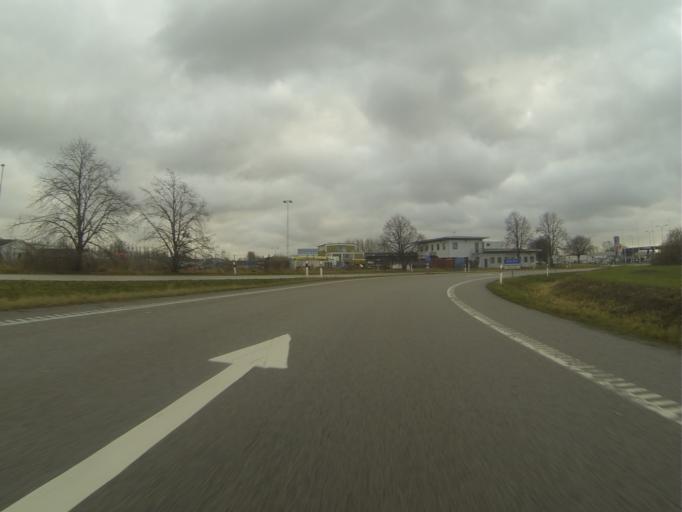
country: SE
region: Skane
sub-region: Burlovs Kommun
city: Arloev
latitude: 55.6473
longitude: 13.0830
